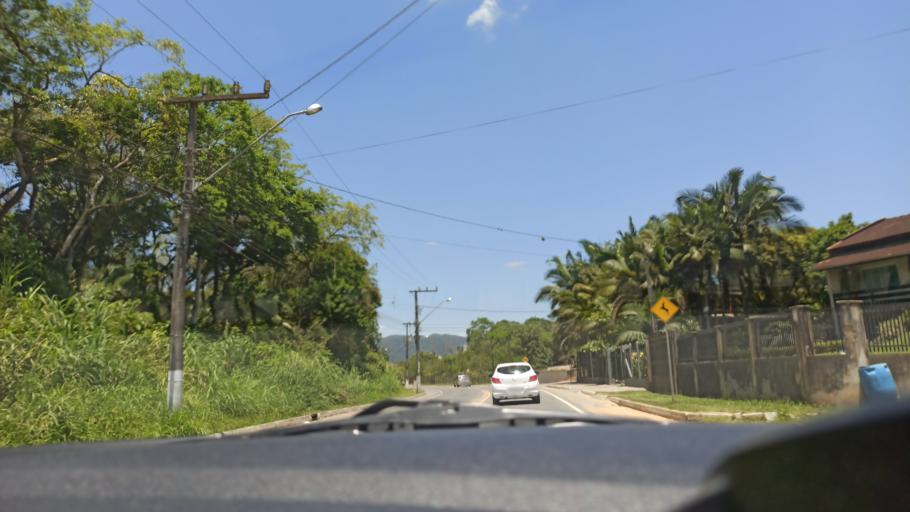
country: BR
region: Santa Catarina
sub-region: Indaial
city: Indaial
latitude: -26.8846
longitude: -49.2406
